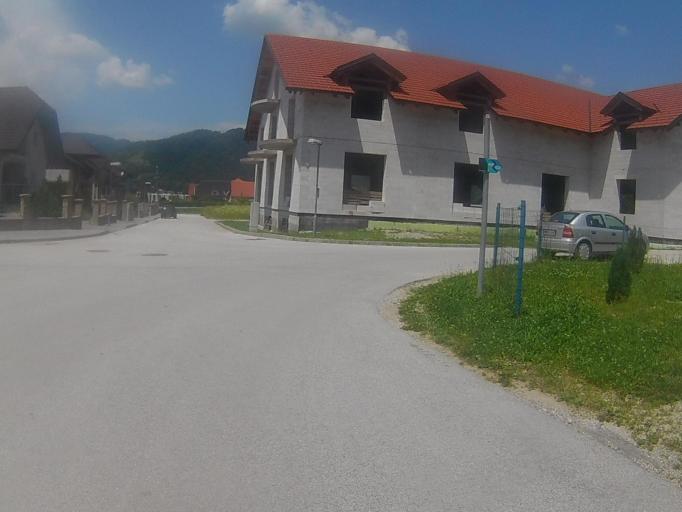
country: SI
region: Ruse
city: Bistrica ob Dravi
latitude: 46.5475
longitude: 15.5351
